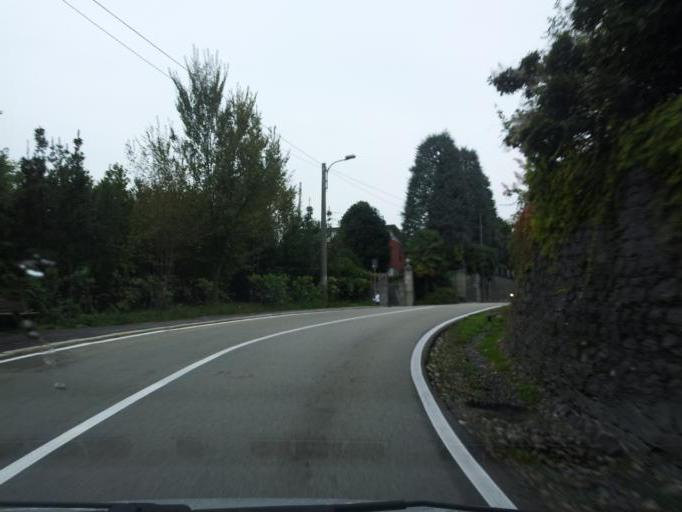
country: IT
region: Lombardy
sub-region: Provincia di Varese
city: Varano Borghi
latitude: 45.7718
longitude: 8.7027
